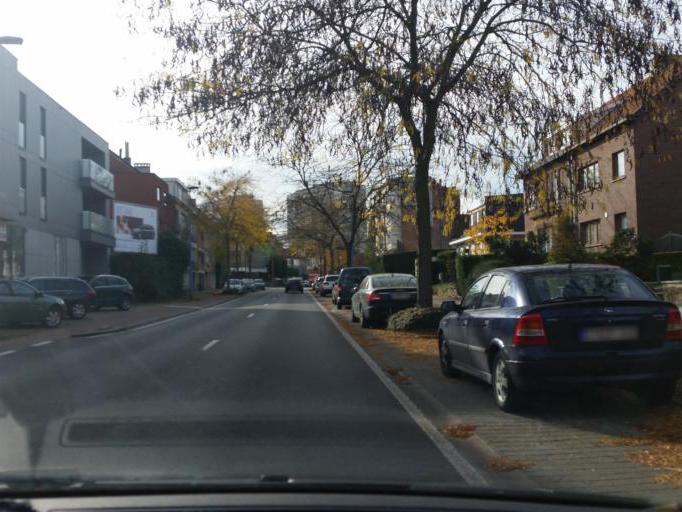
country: BE
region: Flanders
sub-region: Provincie Vlaams-Brabant
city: Grimbergen
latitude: 50.9039
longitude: 4.3625
